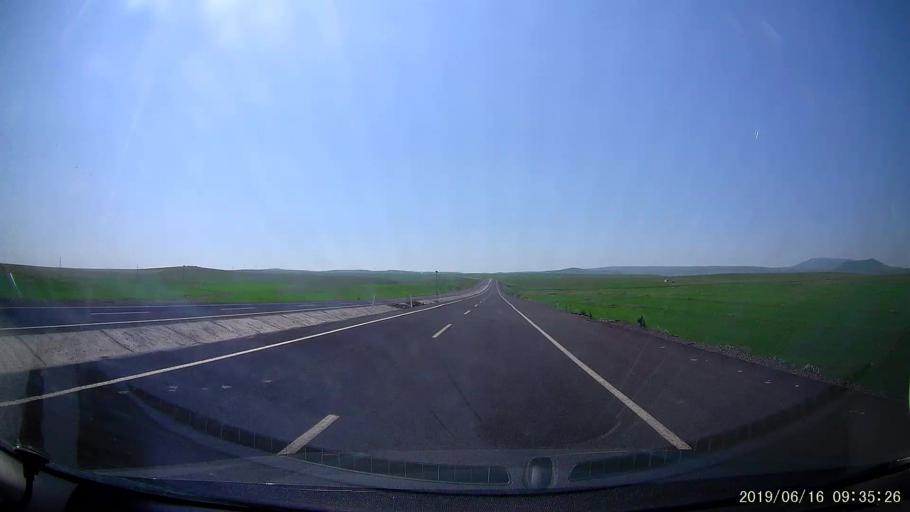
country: TR
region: Kars
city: Kars
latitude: 40.5721
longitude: 43.1558
